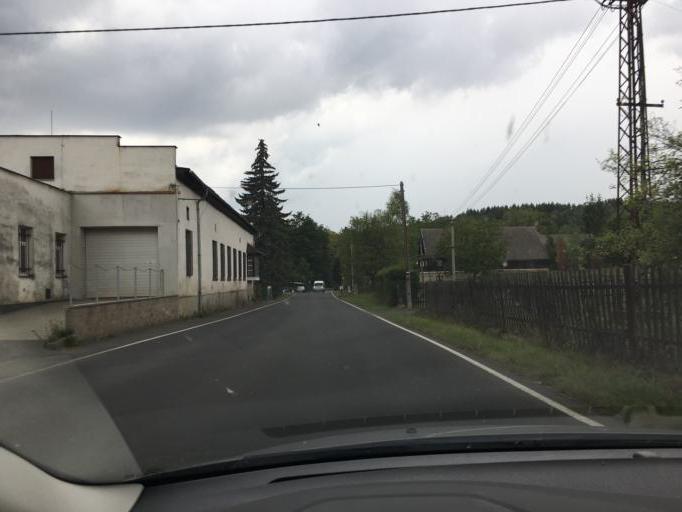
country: CZ
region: Ustecky
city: Ceska Kamenice
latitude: 50.8046
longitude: 14.3645
